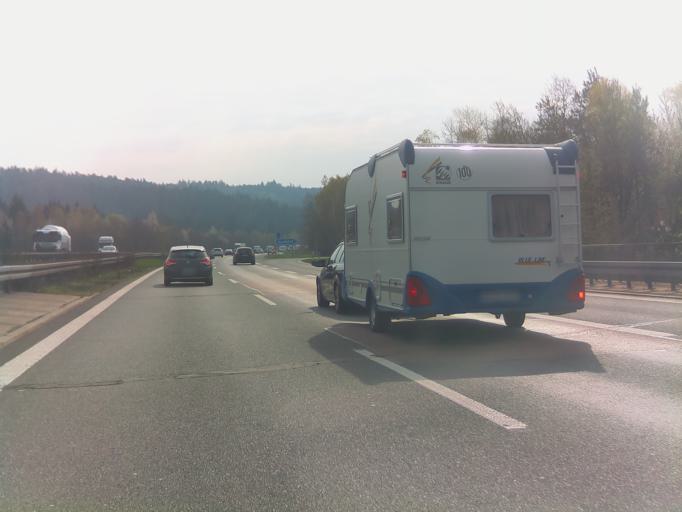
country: DE
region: Bavaria
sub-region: Regierungsbezirk Mittelfranken
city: Schnelldorf
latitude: 49.2111
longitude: 10.1711
